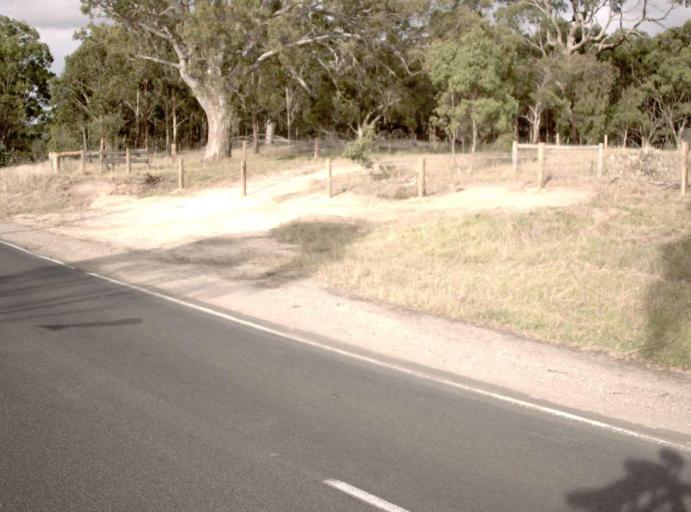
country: AU
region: Victoria
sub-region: Wellington
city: Sale
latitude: -37.9278
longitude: 146.9923
